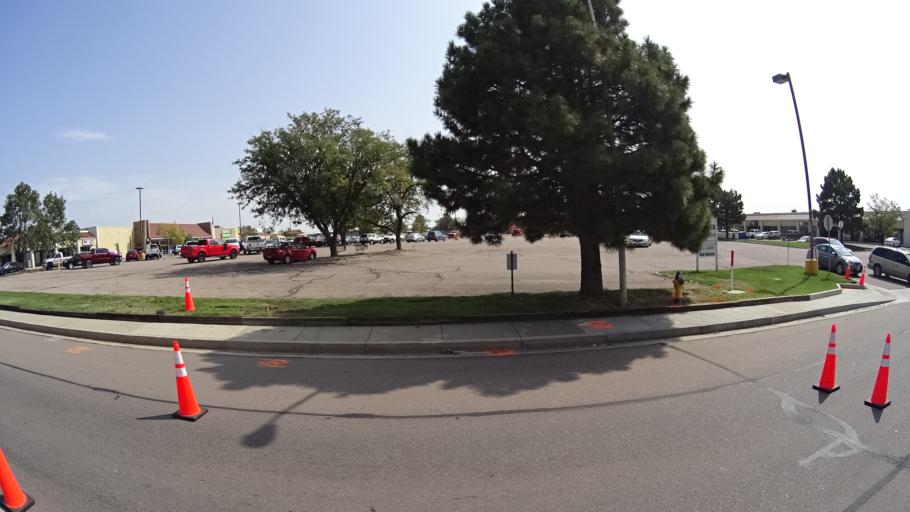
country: US
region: Colorado
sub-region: El Paso County
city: Cimarron Hills
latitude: 38.8422
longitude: -104.7480
